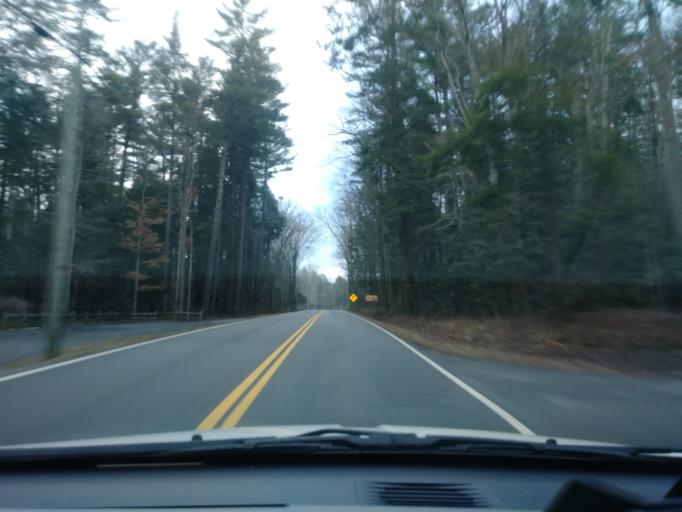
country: US
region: Tennessee
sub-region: Unicoi County
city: Unicoi
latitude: 36.1758
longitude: -82.2977
